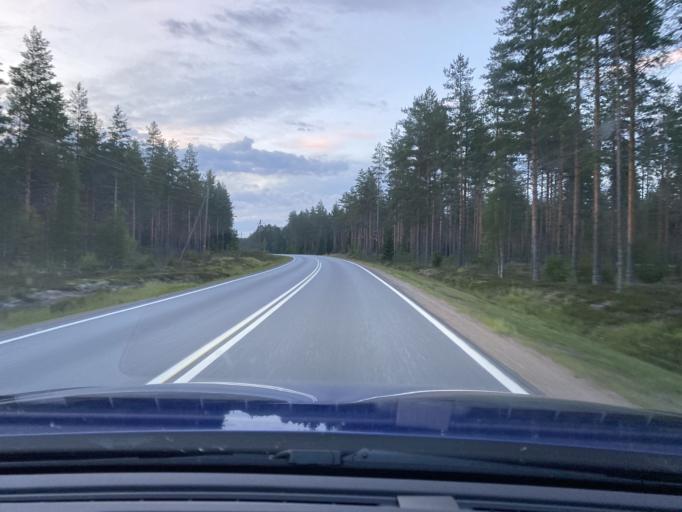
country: FI
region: Satakunta
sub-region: Pohjois-Satakunta
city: Honkajoki
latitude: 62.1504
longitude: 22.2649
